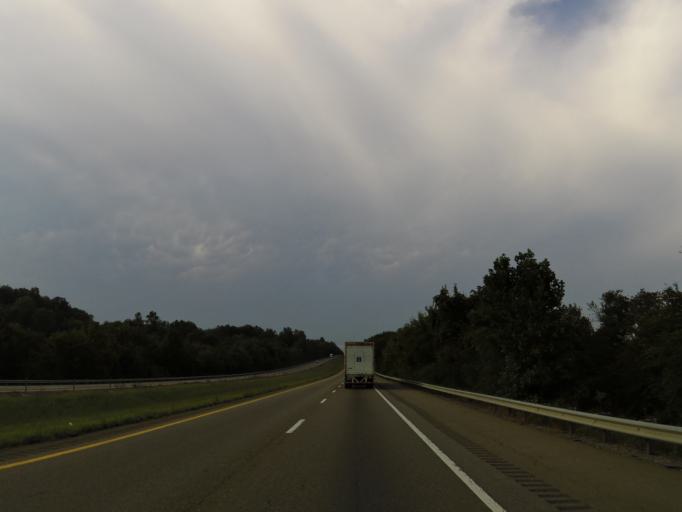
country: US
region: Tennessee
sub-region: Cocke County
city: Newport
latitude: 35.9064
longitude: -83.1847
